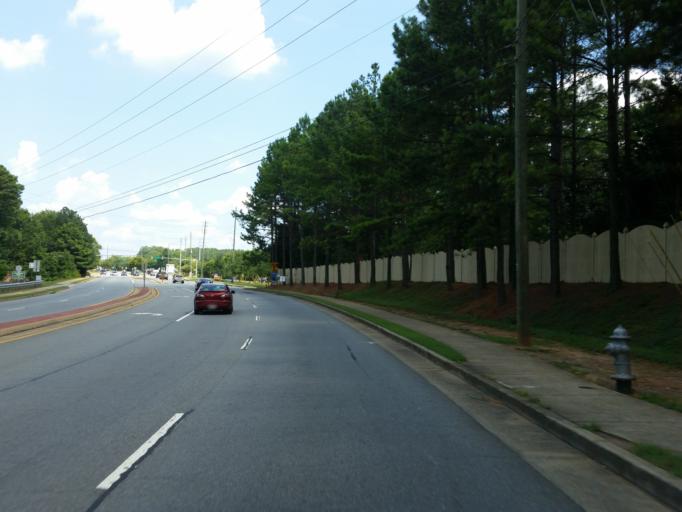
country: US
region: Georgia
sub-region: Cherokee County
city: Woodstock
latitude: 34.0380
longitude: -84.4694
